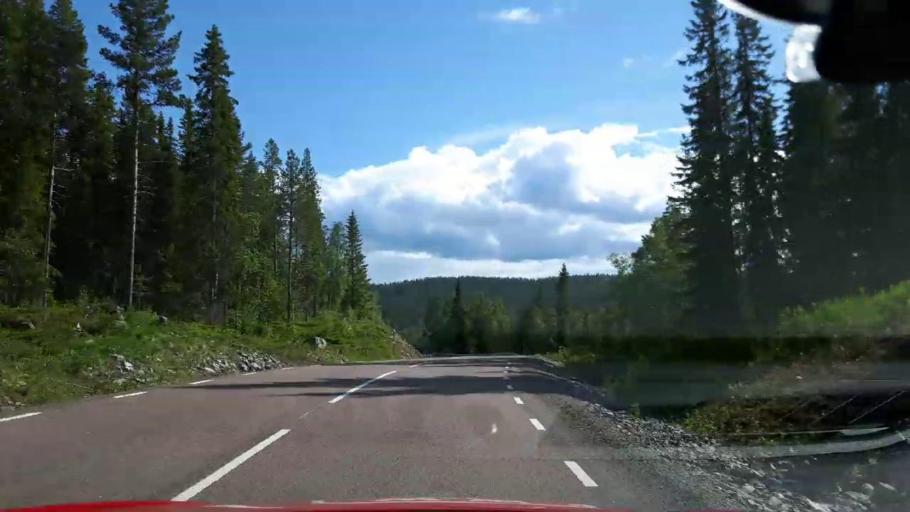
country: SE
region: Jaemtland
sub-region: Krokoms Kommun
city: Valla
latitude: 64.0275
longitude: 14.1982
